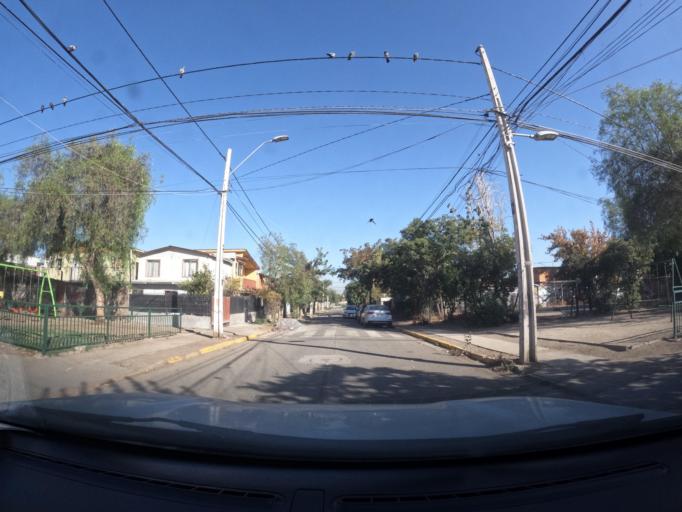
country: CL
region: Santiago Metropolitan
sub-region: Provincia de Santiago
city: Villa Presidente Frei, Nunoa, Santiago, Chile
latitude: -33.5021
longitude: -70.5861
